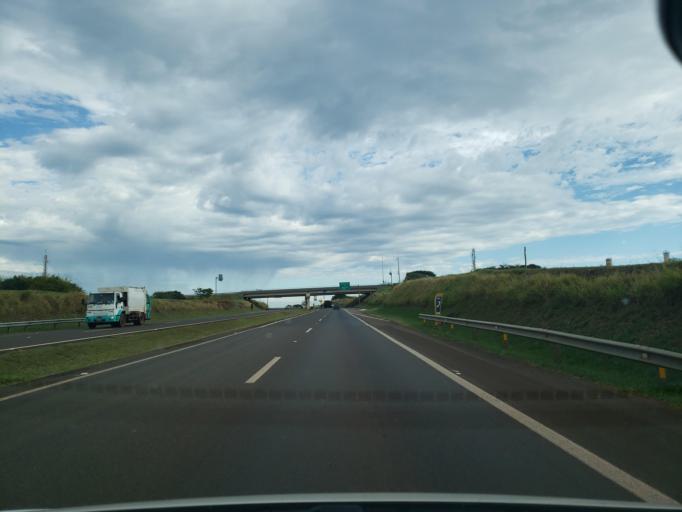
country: BR
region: Sao Paulo
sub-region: Jau
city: Jau
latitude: -22.2573
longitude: -48.5485
